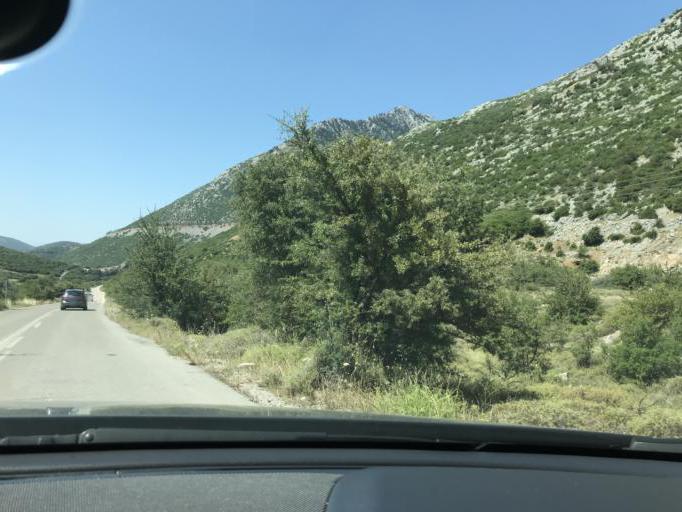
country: GR
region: Central Greece
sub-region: Nomos Voiotias
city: Distomo
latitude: 38.4825
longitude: 22.6876
